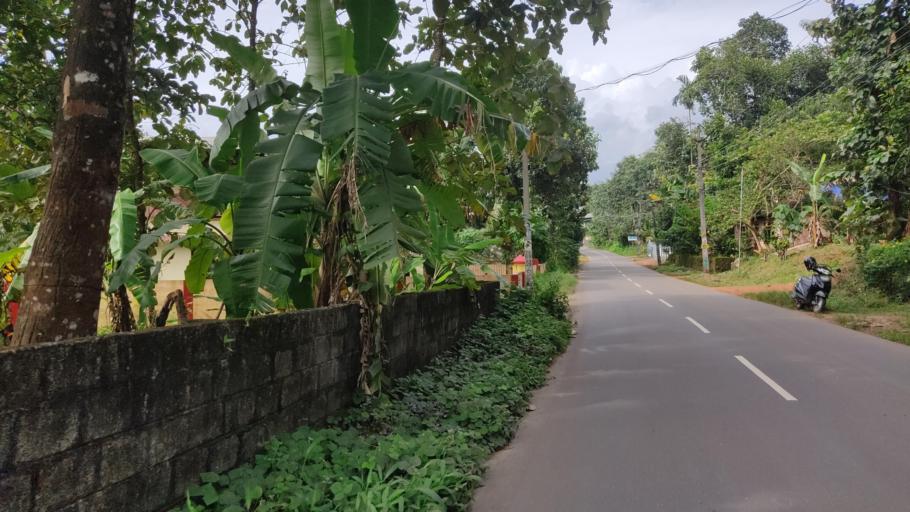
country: IN
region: Kerala
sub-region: Pattanamtitta
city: Adur
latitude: 9.1920
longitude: 76.7753
